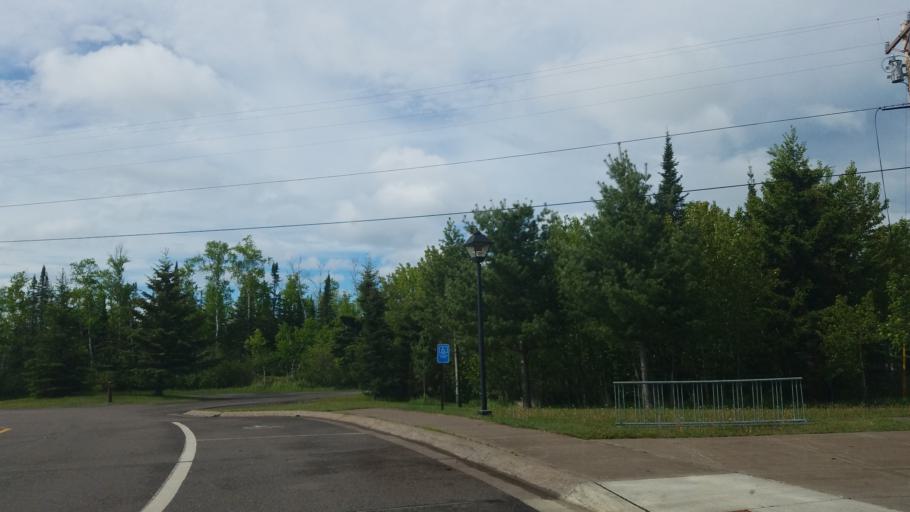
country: US
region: Minnesota
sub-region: Lake County
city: Silver Bay
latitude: 47.2029
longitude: -91.3698
